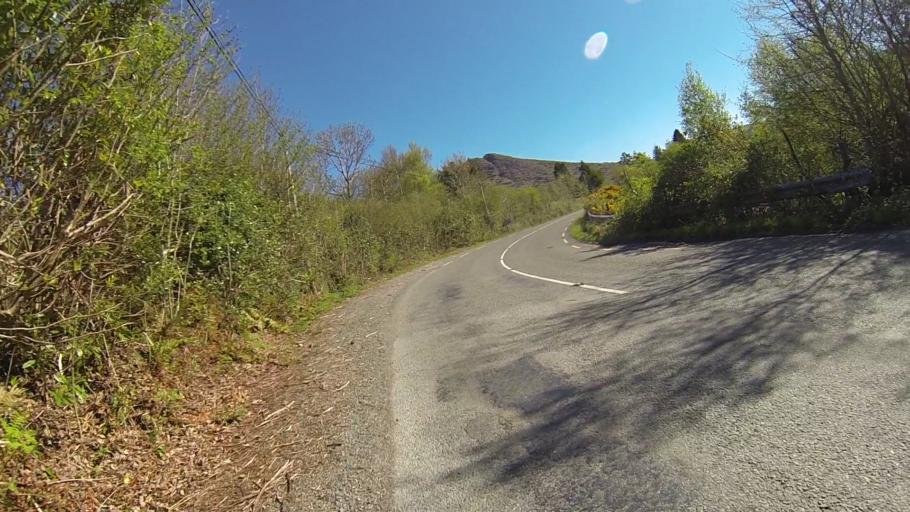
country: IE
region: Munster
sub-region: Ciarrai
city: Kenmare
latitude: 51.7704
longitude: -9.7545
